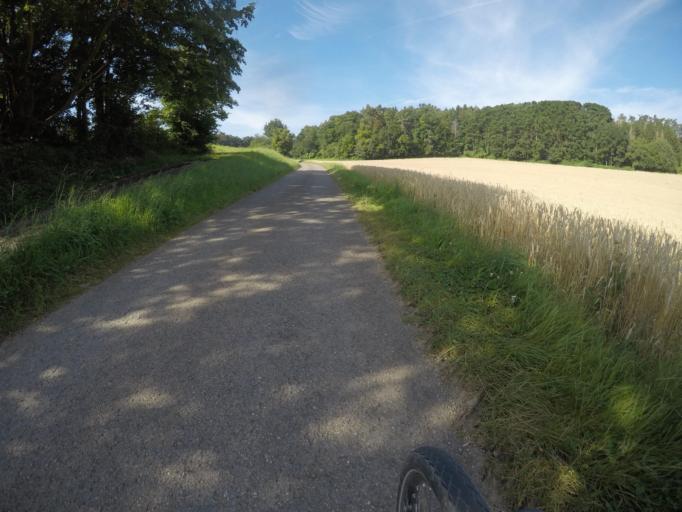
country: DE
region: Baden-Wuerttemberg
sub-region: Karlsruhe Region
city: Monsheim
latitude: 48.8818
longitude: 8.8796
